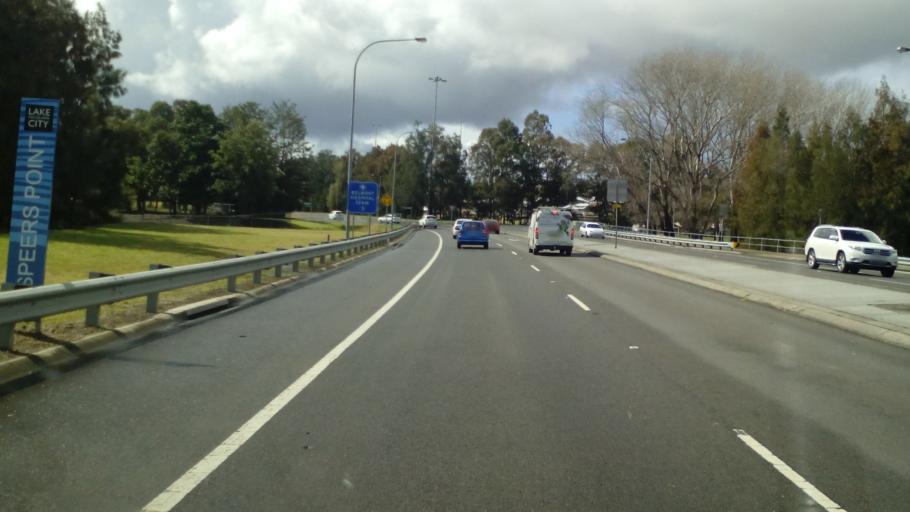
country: AU
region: New South Wales
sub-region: Lake Macquarie Shire
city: Glendale
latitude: -32.9583
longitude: 151.6159
